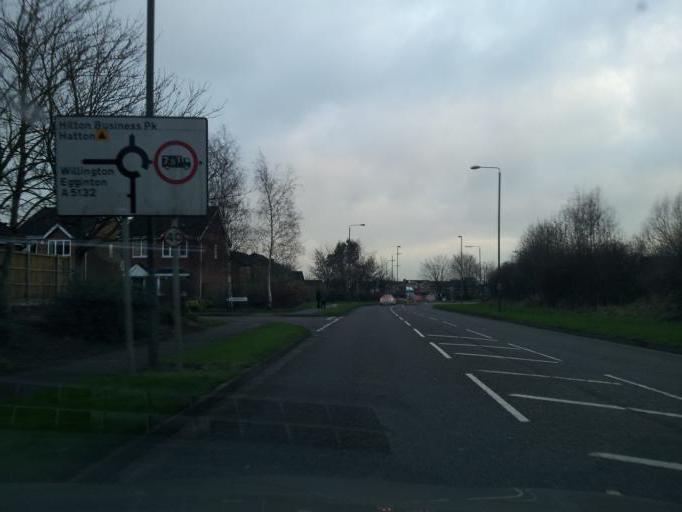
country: GB
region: England
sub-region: Derbyshire
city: Etwall
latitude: 52.8732
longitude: -1.6280
